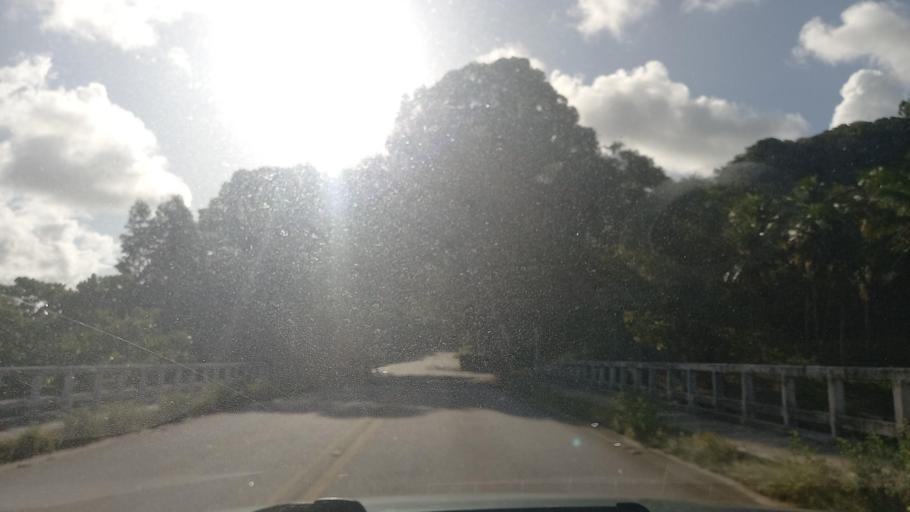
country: BR
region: Alagoas
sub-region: Marechal Deodoro
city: Marechal Deodoro
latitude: -9.8373
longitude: -35.9275
